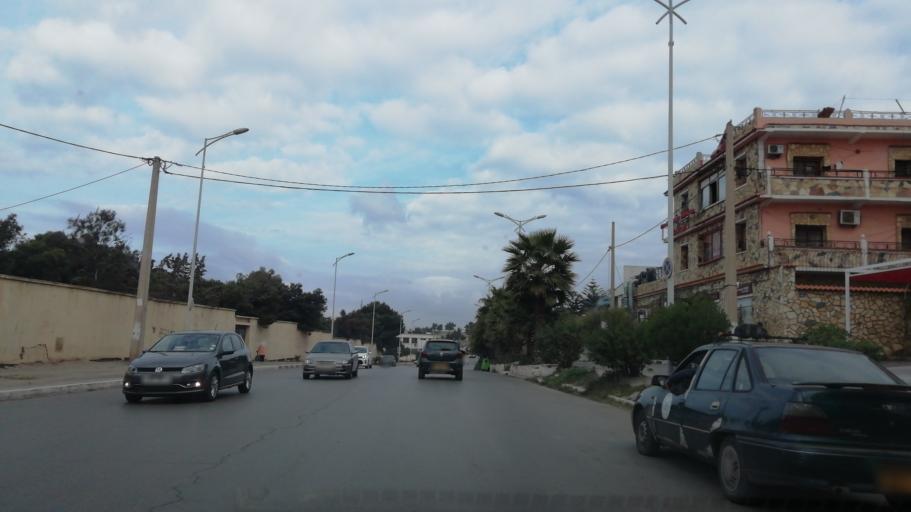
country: DZ
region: Oran
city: Oran
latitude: 35.7124
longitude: -0.6119
